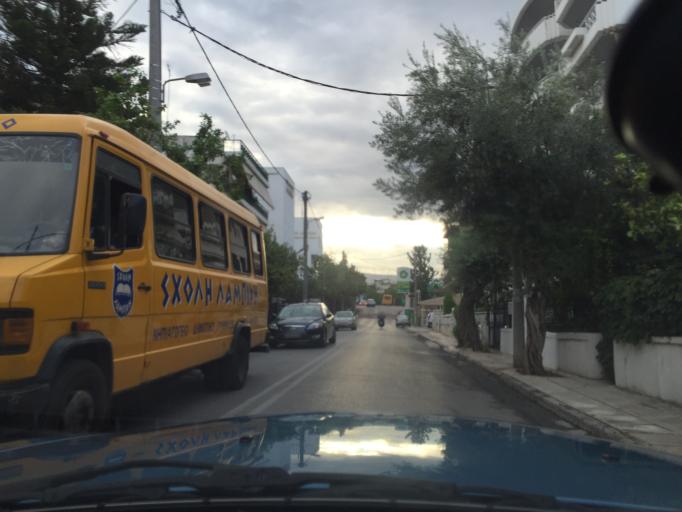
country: GR
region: Attica
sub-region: Nomarchia Athinas
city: Moskhaton
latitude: 37.9506
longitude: 23.6848
